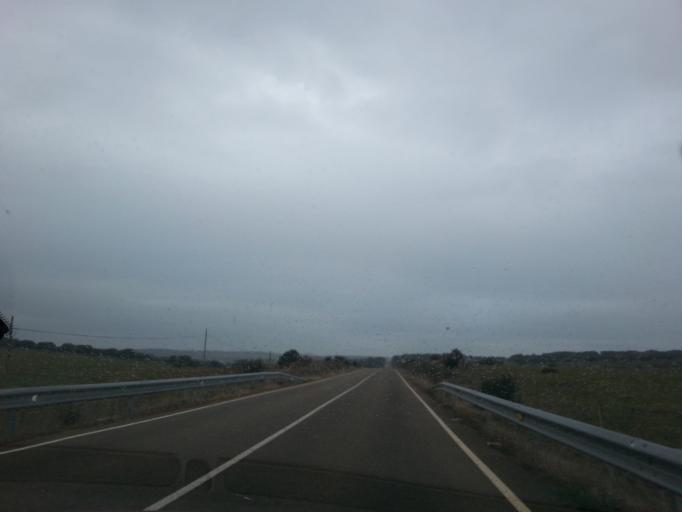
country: ES
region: Castille and Leon
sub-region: Provincia de Salamanca
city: Tamames
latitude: 40.6738
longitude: -6.0751
